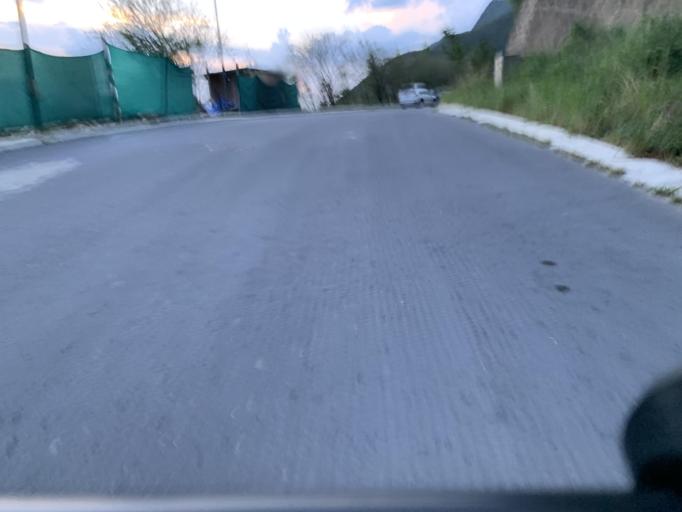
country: MX
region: Nuevo Leon
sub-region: Juarez
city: Bosques de San Pedro
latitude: 25.5215
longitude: -100.1876
